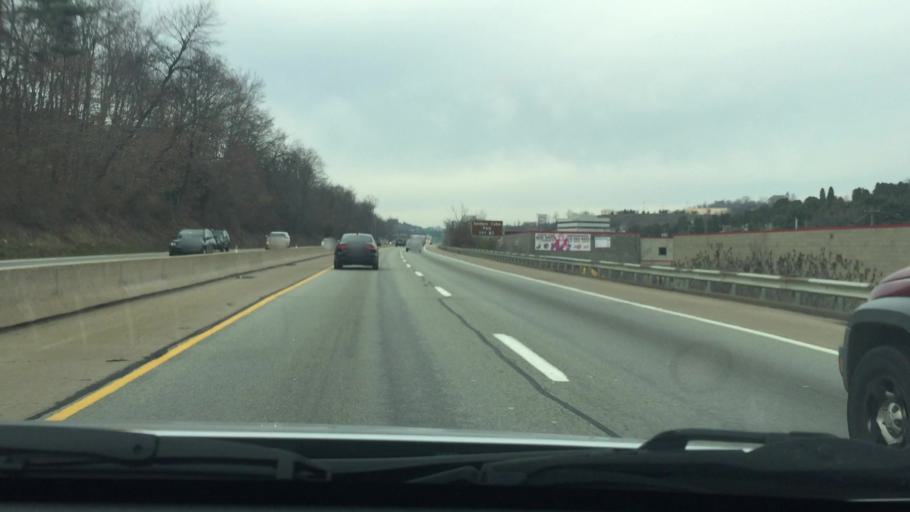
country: US
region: Pennsylvania
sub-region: Allegheny County
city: Rennerdale
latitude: 40.4317
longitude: -80.1384
